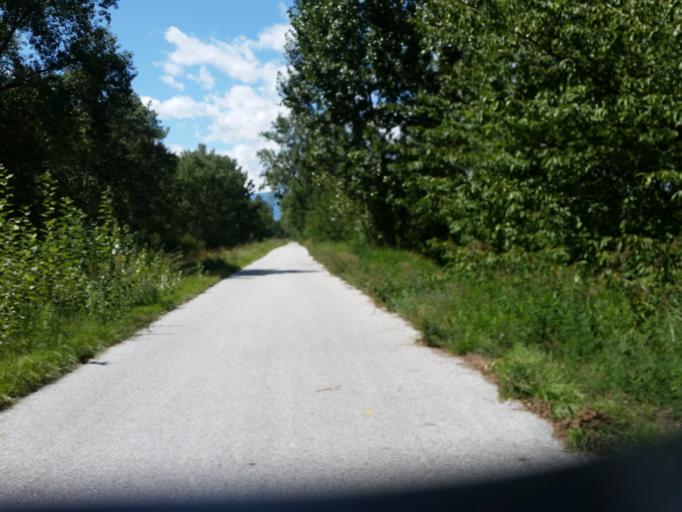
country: CH
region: Valais
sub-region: Conthey District
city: Ardon
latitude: 46.1963
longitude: 7.2740
